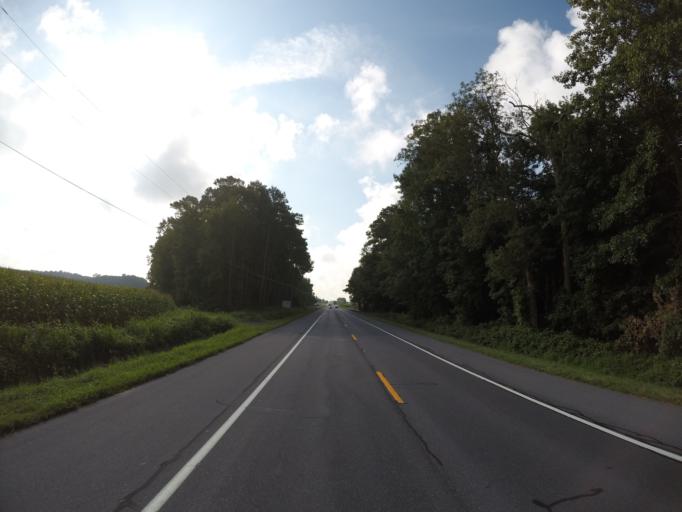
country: US
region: Delaware
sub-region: Sussex County
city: Bridgeville
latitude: 38.7775
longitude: -75.6628
